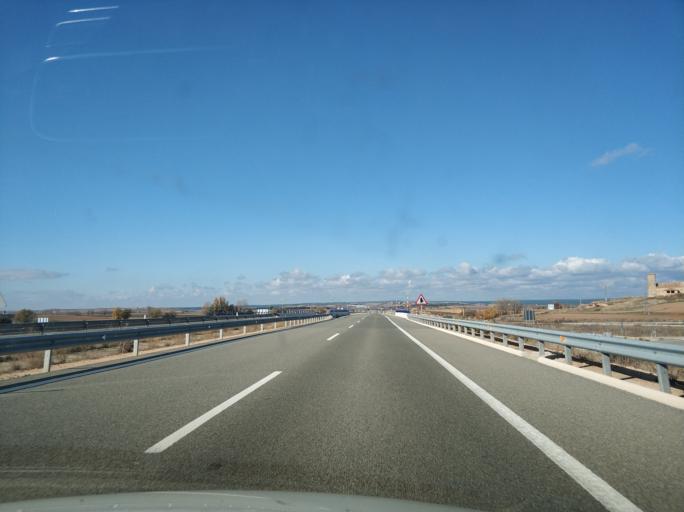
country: ES
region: Castille and Leon
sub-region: Provincia de Soria
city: Frechilla de Almazan
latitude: 41.4461
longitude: -2.5063
